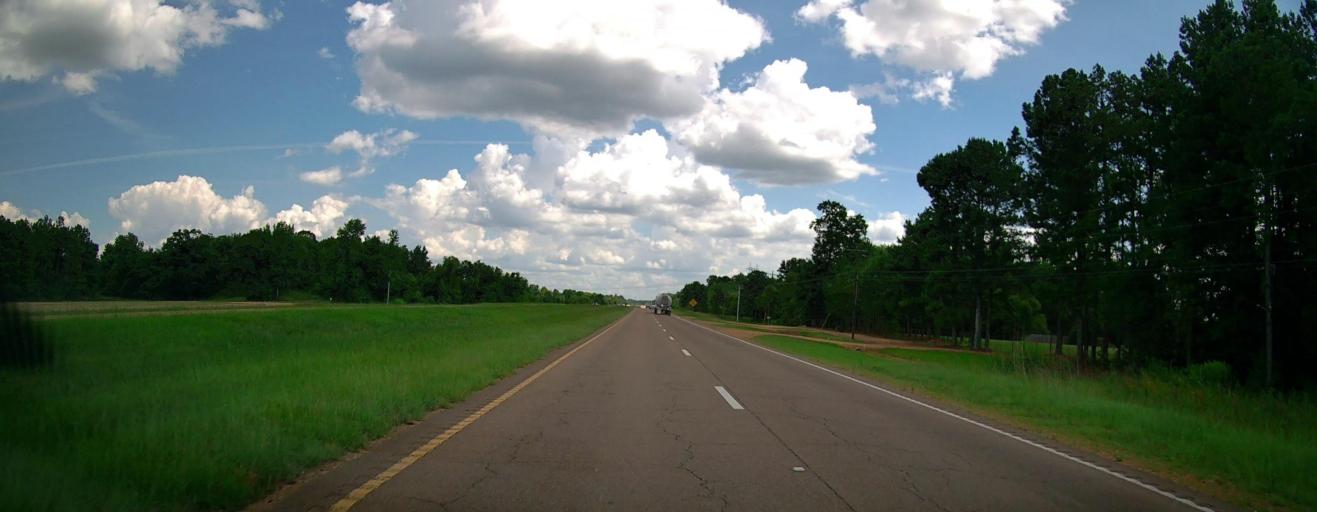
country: US
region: Mississippi
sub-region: Lowndes County
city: Columbus Air Force Base
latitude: 33.6836
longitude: -88.4349
